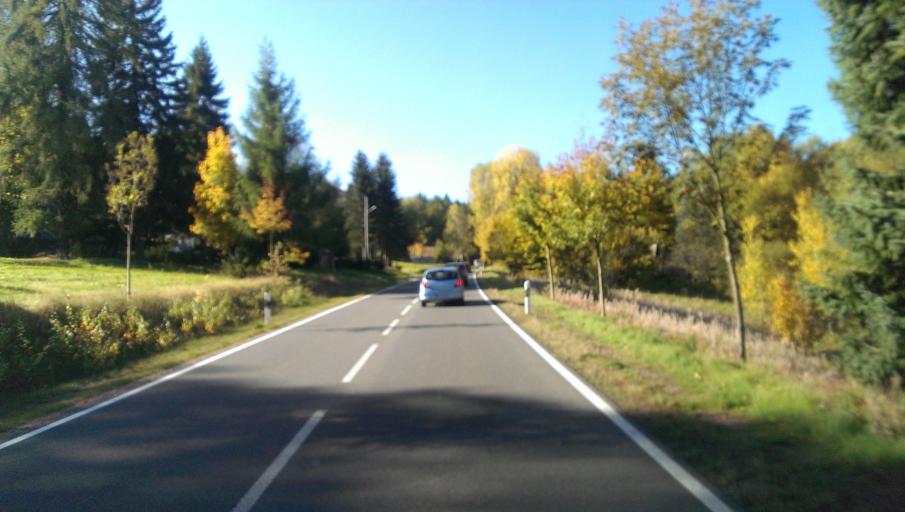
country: DE
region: Saxony
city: Geising
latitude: 50.7591
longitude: 13.7807
